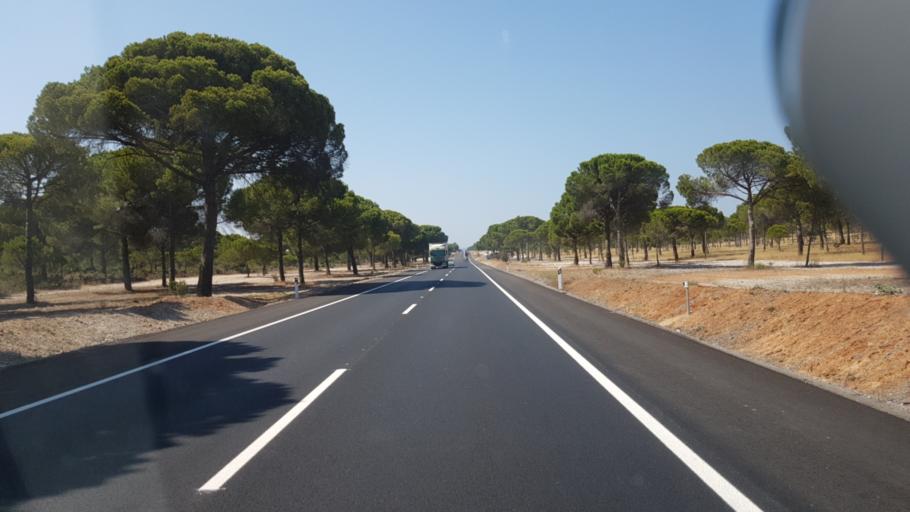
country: PT
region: Setubal
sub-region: Grandola
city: Grandola
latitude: 38.2636
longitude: -8.5439
